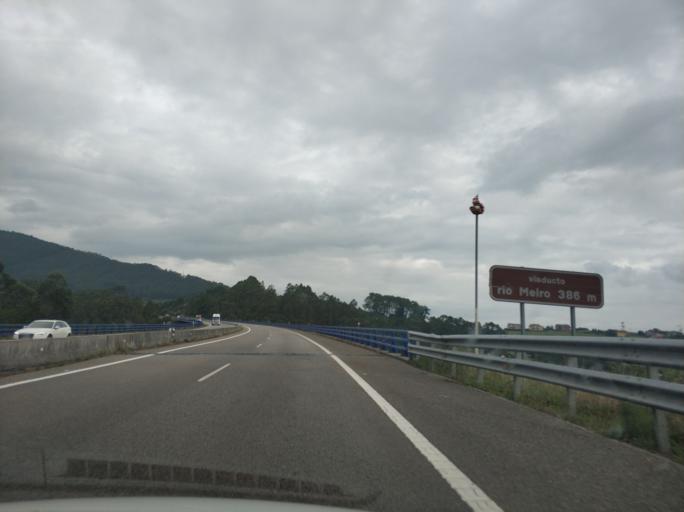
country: ES
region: Asturias
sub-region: Province of Asturias
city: Navia
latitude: 43.5317
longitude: -6.7312
